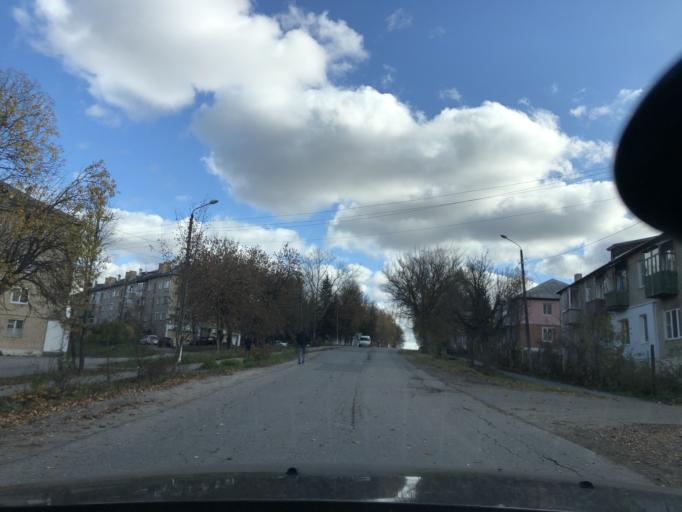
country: RU
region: Tula
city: Gorelki
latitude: 54.2959
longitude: 37.5682
